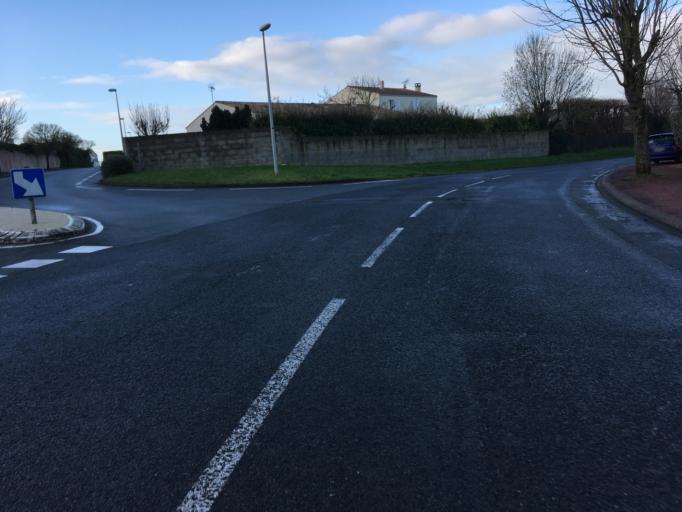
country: FR
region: Poitou-Charentes
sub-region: Departement de la Charente-Maritime
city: Nieul-sur-Mer
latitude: 46.2041
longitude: -1.1711
